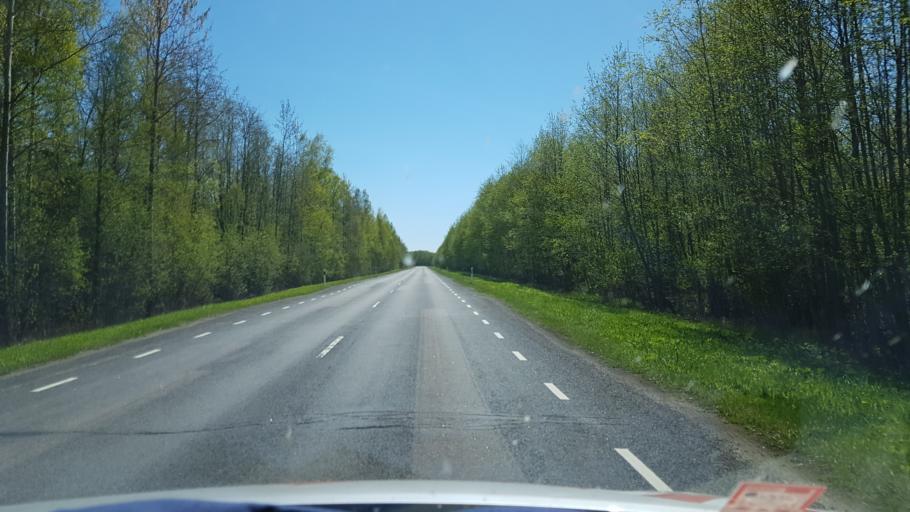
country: EE
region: Ida-Virumaa
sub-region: Sillamaee linn
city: Sillamae
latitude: 59.3163
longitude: 27.9138
